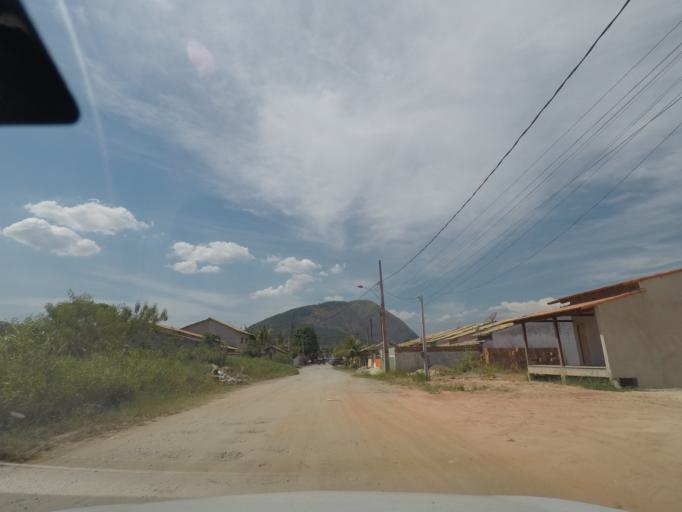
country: BR
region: Rio de Janeiro
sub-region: Marica
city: Marica
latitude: -22.9580
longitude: -42.9640
